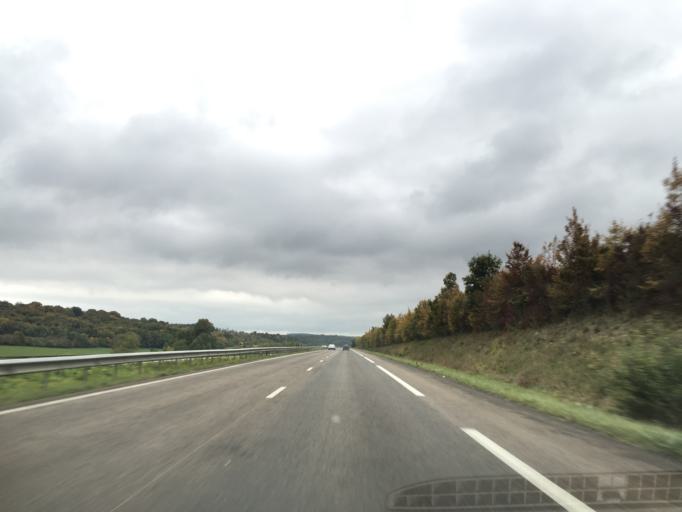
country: FR
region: Lorraine
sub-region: Departement de la Meuse
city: Vacon
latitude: 48.6866
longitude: 5.5904
